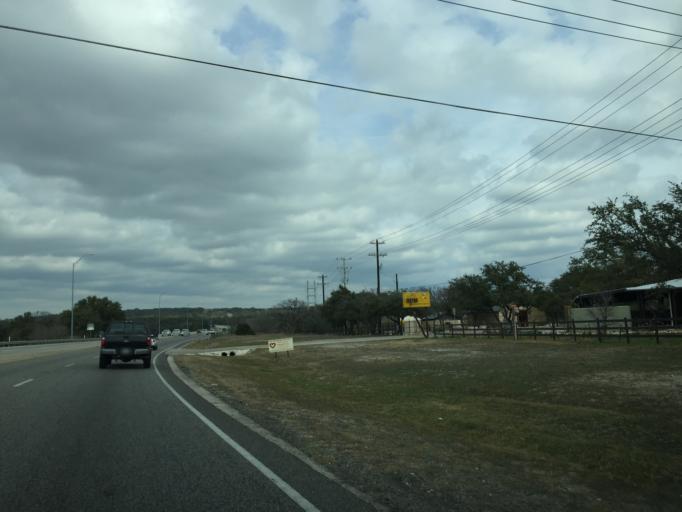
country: US
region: Texas
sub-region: Travis County
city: Briarcliff
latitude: 30.3864
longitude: -98.0862
